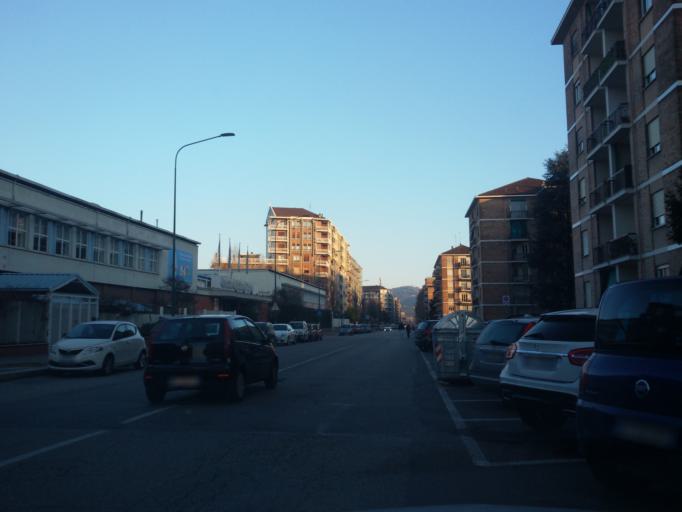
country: IT
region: Piedmont
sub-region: Provincia di Torino
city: Lesna
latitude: 45.0452
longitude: 7.6359
